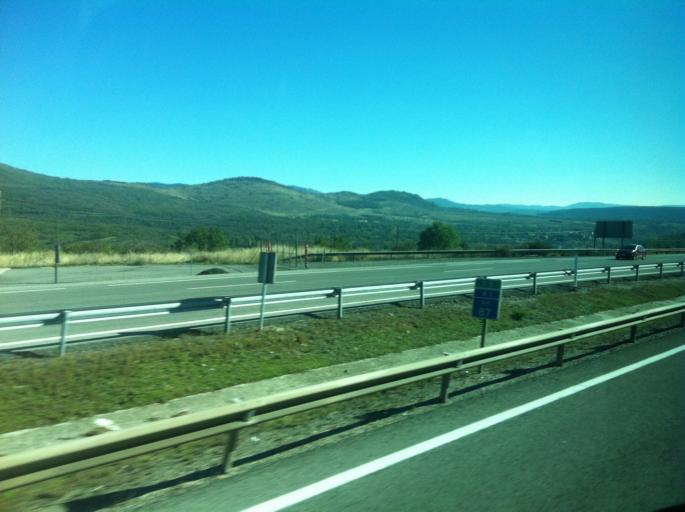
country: ES
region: Madrid
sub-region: Provincia de Madrid
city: Robregordo
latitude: 41.0893
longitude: -3.5955
